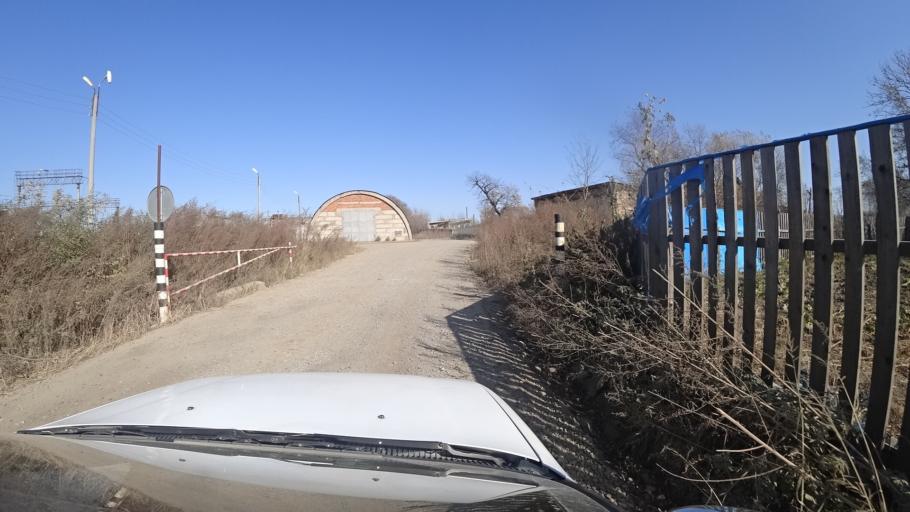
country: RU
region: Primorskiy
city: Dal'nerechensk
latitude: 45.9324
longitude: 133.7176
